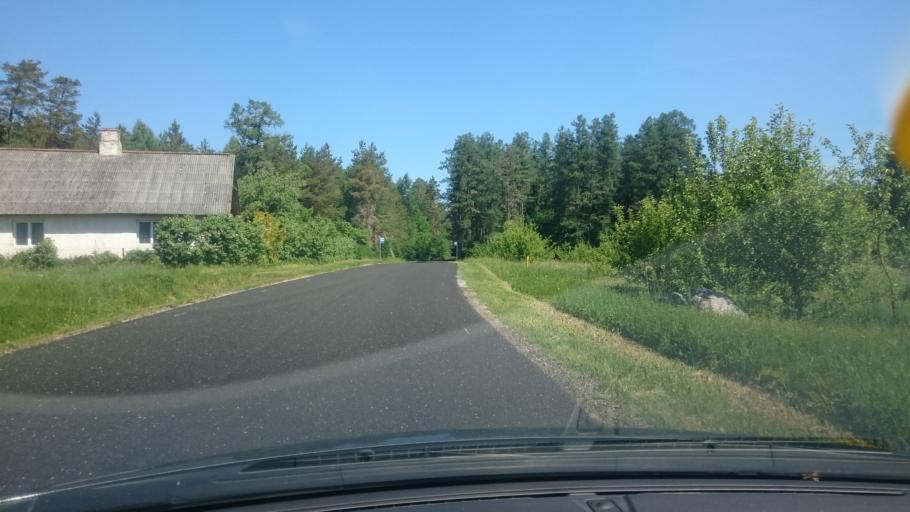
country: EE
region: Harju
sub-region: Rae vald
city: Vaida
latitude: 59.2142
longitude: 24.9522
